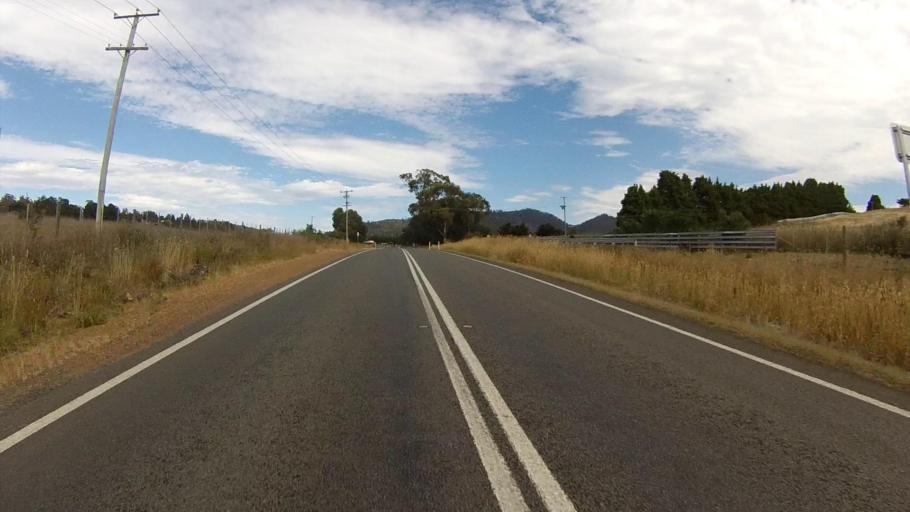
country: AU
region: Tasmania
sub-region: Brighton
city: Old Beach
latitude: -42.6713
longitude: 147.3912
